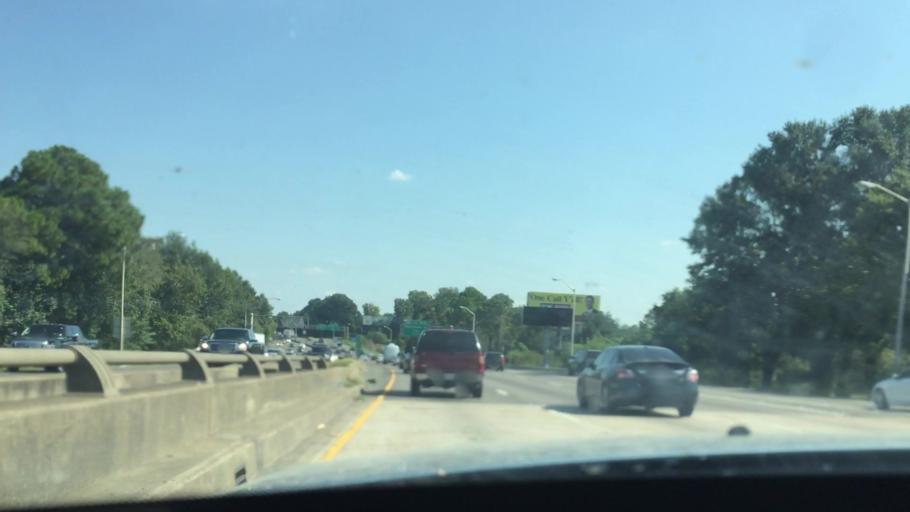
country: US
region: Louisiana
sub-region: East Baton Rouge Parish
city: Baton Rouge
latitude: 30.4308
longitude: -91.1741
